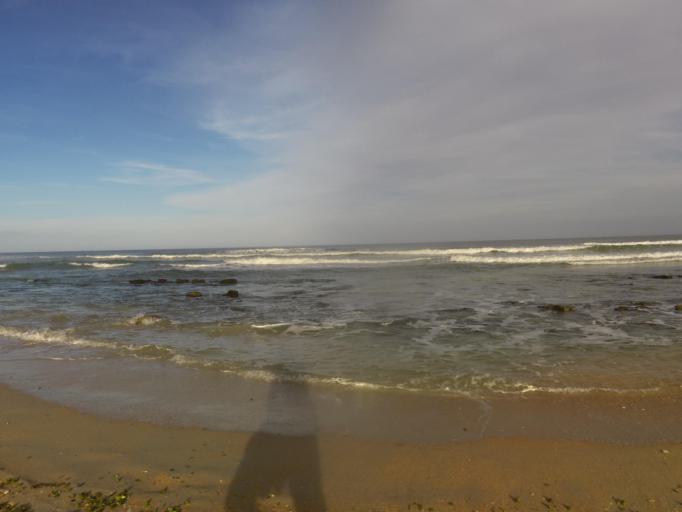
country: US
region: Florida
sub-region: Flagler County
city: Palm Coast
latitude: 29.6154
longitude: -81.1894
